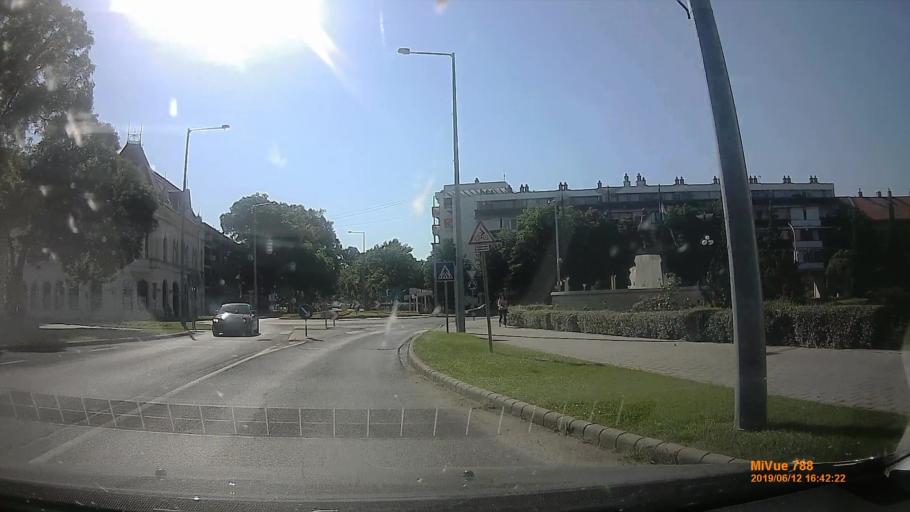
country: HU
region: Csongrad
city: Mako
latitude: 46.2147
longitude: 20.4788
